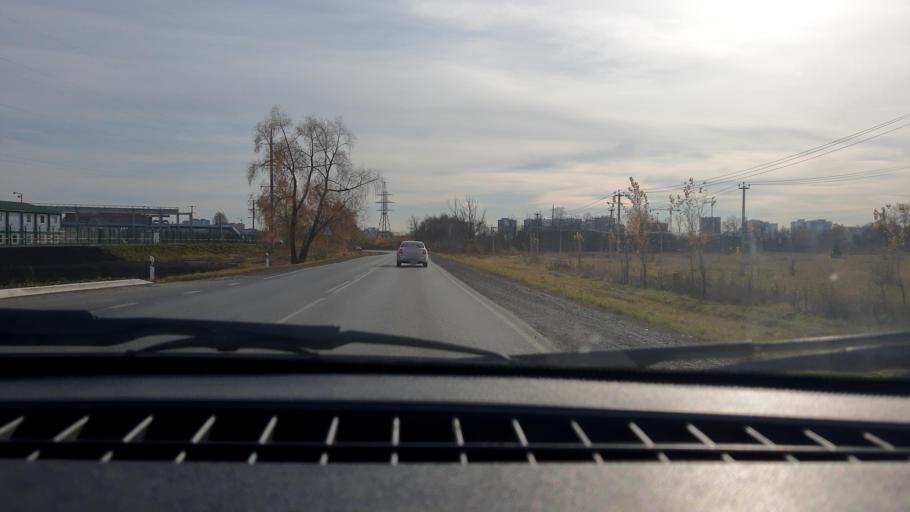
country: RU
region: Bashkortostan
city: Mikhaylovka
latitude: 54.8008
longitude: 55.8346
